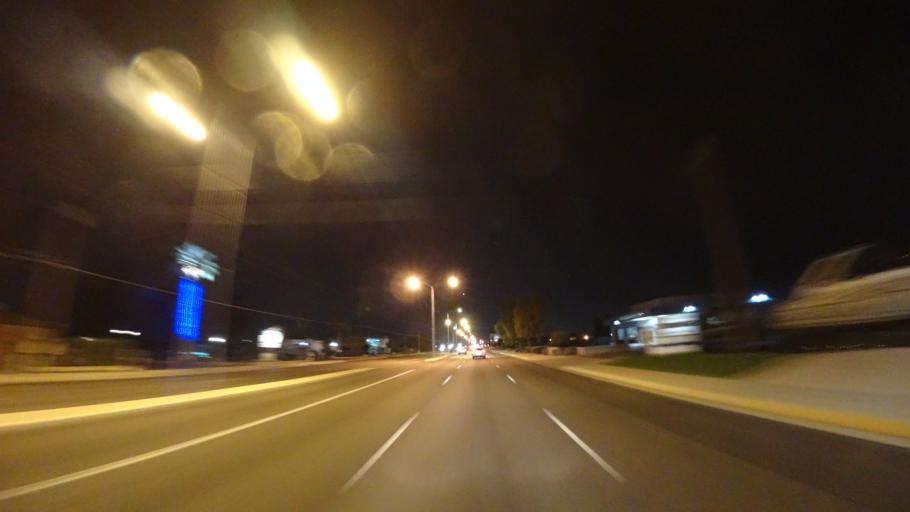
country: US
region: Arizona
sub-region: Maricopa County
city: Mesa
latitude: 33.4156
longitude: -111.7598
